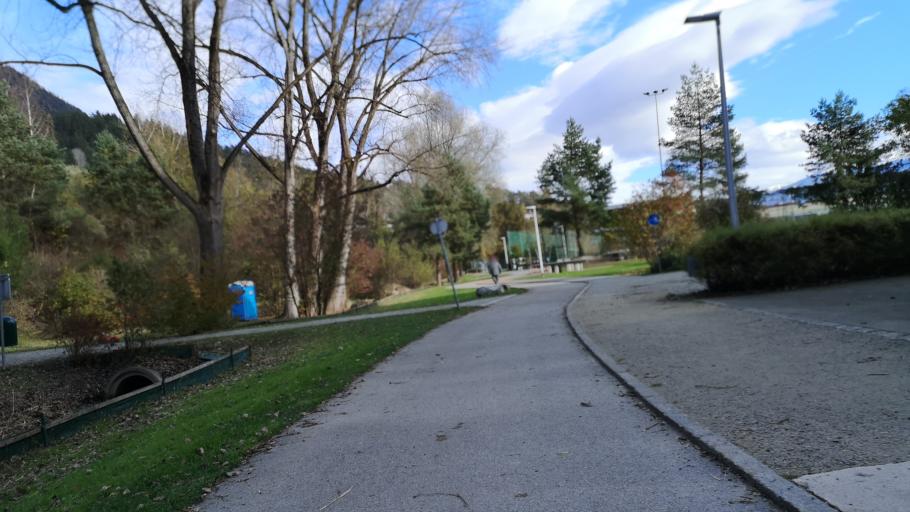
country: AT
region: Tyrol
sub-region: Politischer Bezirk Innsbruck Land
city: Vols
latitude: 47.2670
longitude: 11.3414
